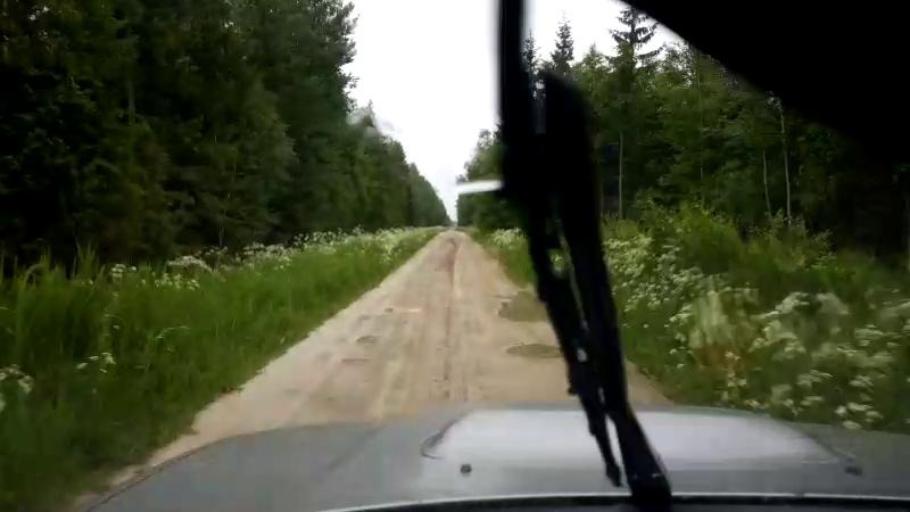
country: EE
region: Paernumaa
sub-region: Halinga vald
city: Parnu-Jaagupi
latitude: 58.5849
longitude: 24.6358
